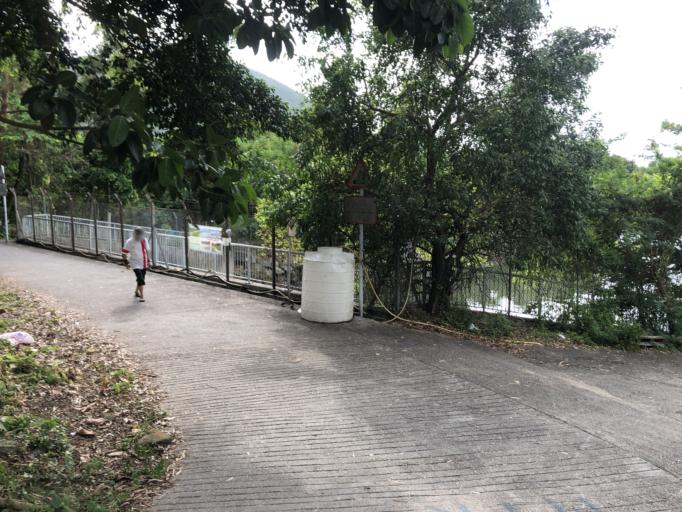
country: HK
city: Tai O
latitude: 22.2793
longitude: 113.9341
